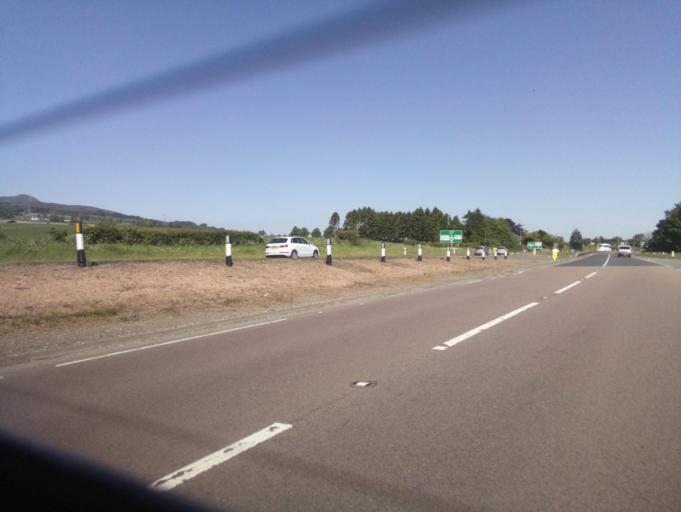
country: GB
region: Scotland
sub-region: Fife
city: Freuchie
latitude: 56.2303
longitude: -3.1541
